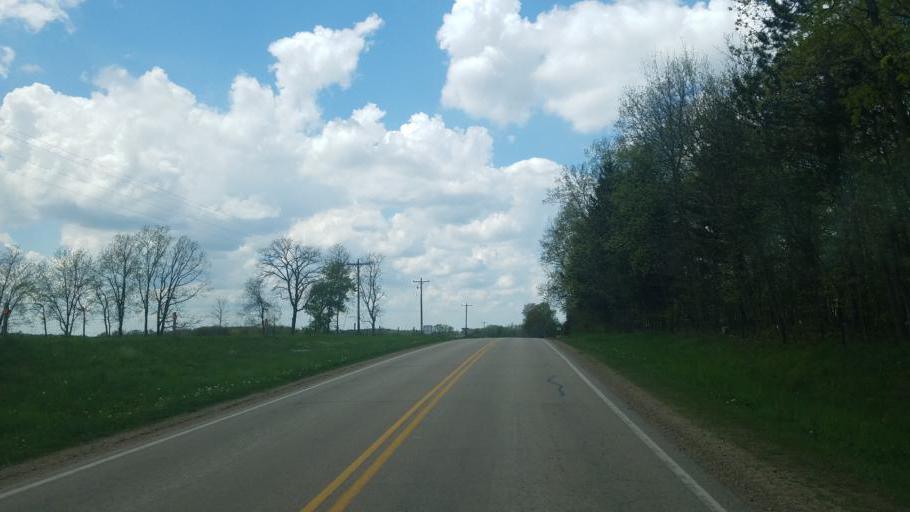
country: US
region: Wisconsin
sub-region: Vernon County
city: Hillsboro
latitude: 43.5937
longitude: -90.3103
